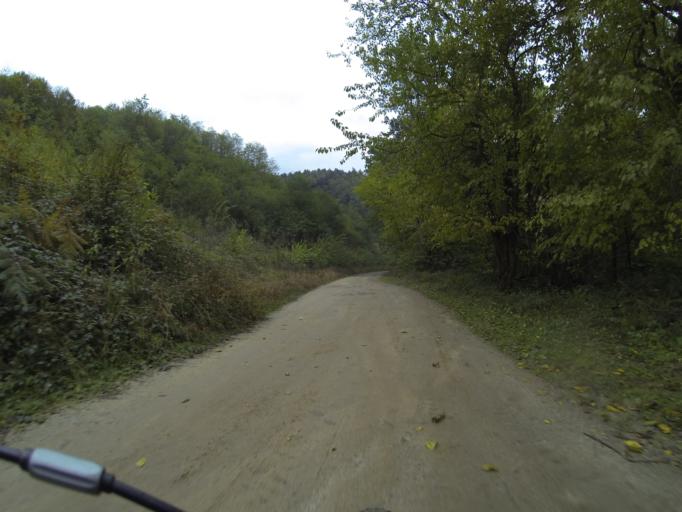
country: RO
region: Gorj
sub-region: Comuna Tismana
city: Sohodol
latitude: 45.0571
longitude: 22.9039
